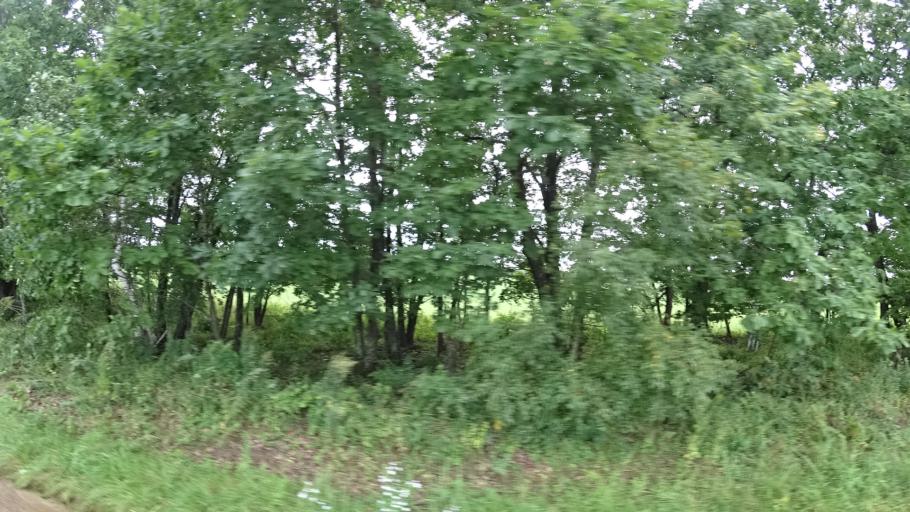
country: RU
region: Primorskiy
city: Rettikhovka
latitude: 44.0675
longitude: 132.6458
